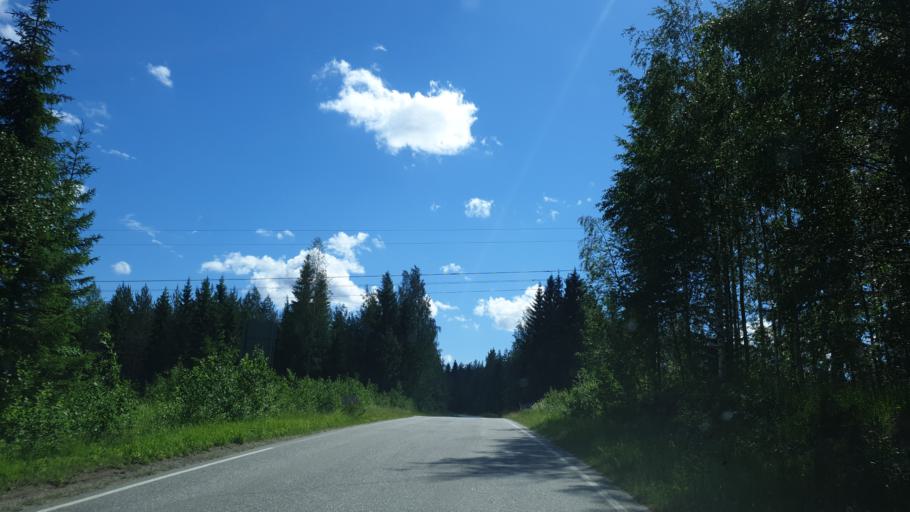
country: FI
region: Northern Savo
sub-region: Koillis-Savo
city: Kaavi
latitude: 63.0027
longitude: 28.5018
